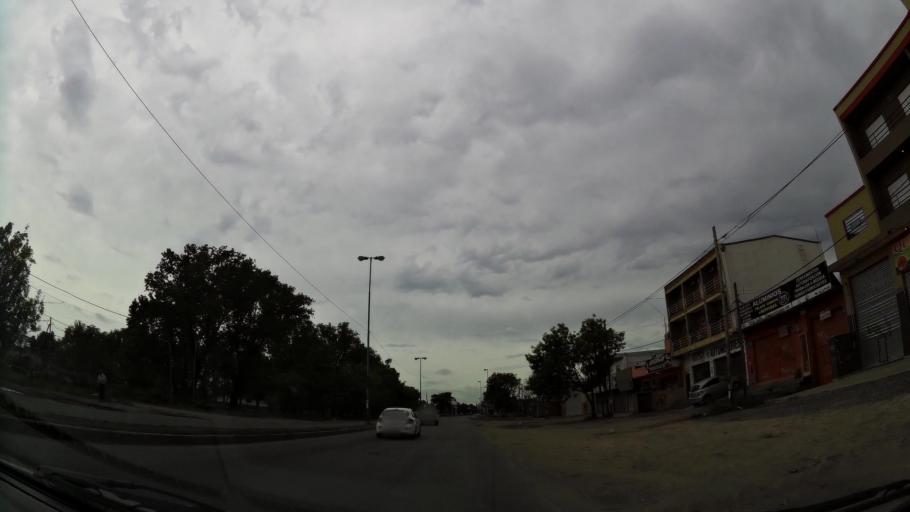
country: AR
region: Buenos Aires
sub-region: Partido de Quilmes
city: Quilmes
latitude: -34.7868
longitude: -58.2789
